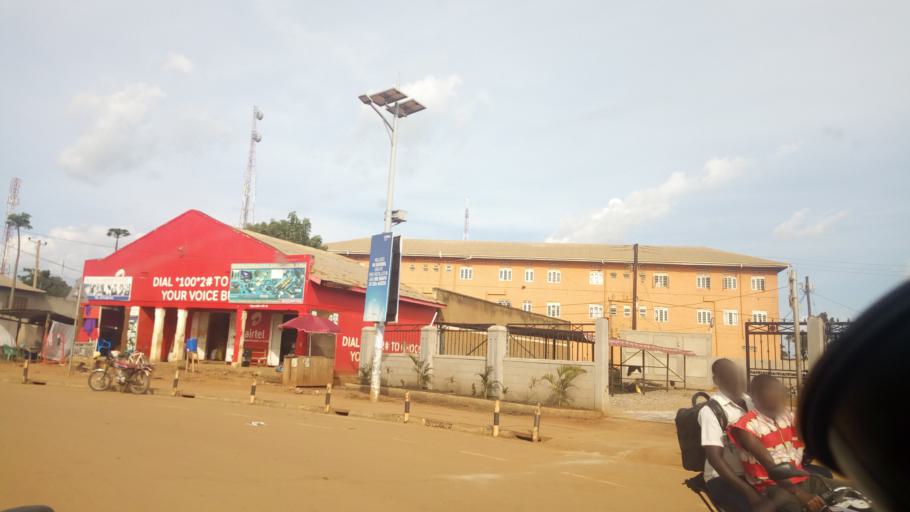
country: UG
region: Northern Region
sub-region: Lira District
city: Lira
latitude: 2.2374
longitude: 32.8917
